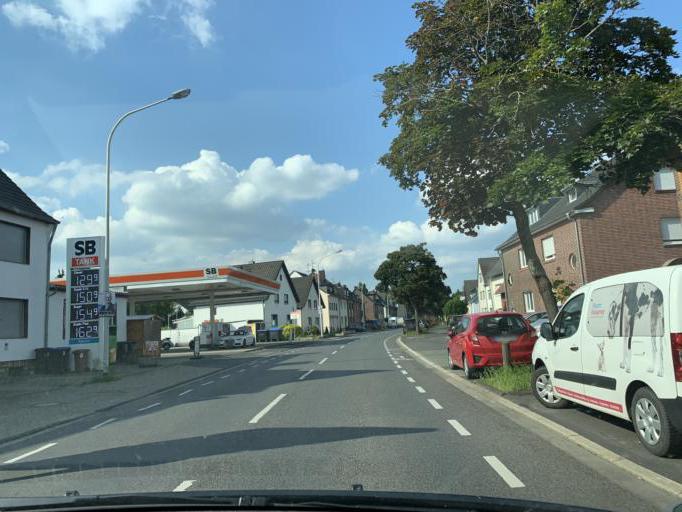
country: DE
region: North Rhine-Westphalia
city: Bruhl
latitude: 50.8366
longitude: 6.8966
